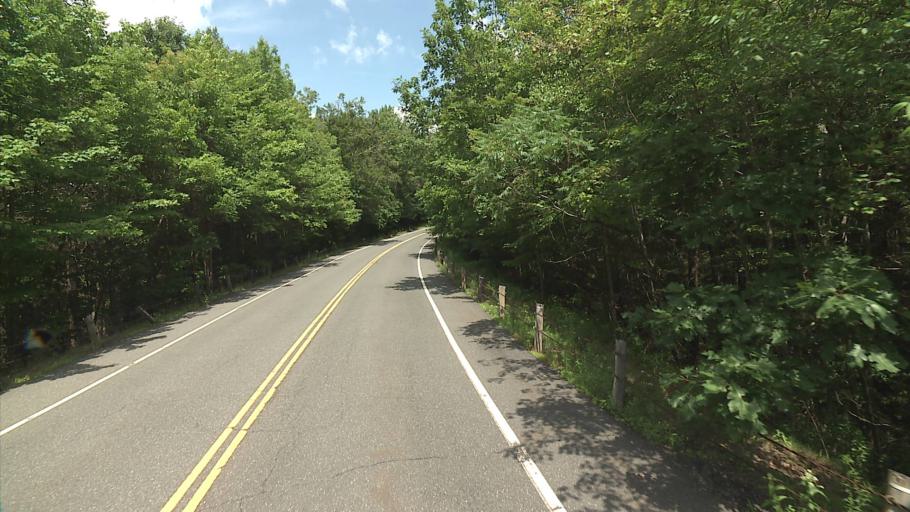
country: US
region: Massachusetts
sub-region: Hampden County
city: Granville
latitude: 42.0267
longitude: -72.9663
